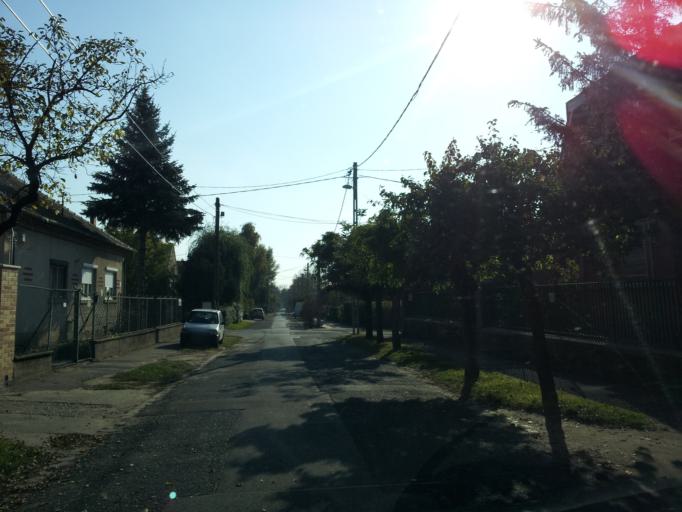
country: HU
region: Budapest
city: Budapest XVIII. keruelet
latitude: 47.4609
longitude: 19.1864
